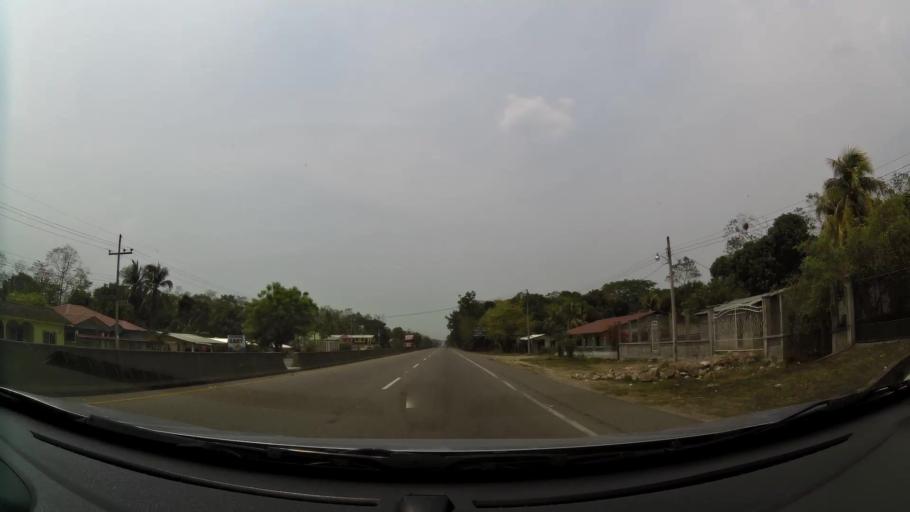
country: HN
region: Cortes
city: Oropendolas
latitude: 15.0556
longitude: -87.9287
